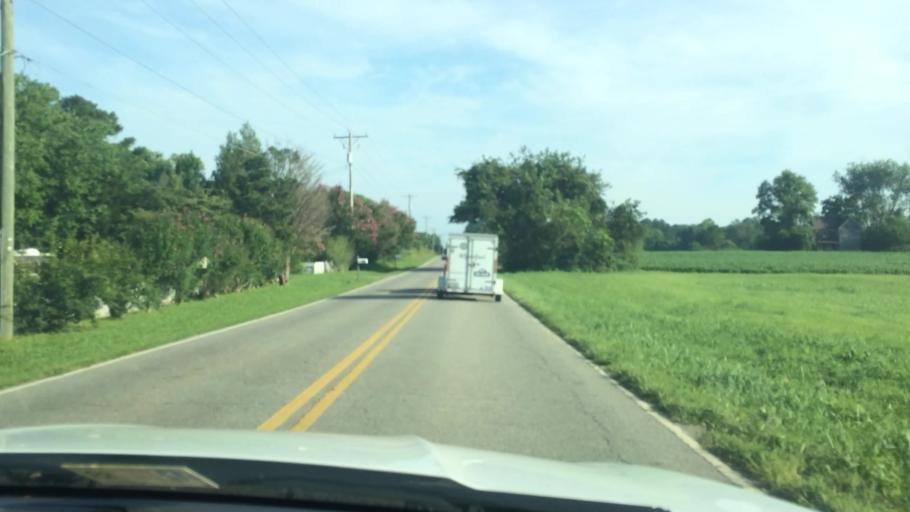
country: US
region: Virginia
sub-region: Middlesex County
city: Deltaville
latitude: 37.5686
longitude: -76.4533
